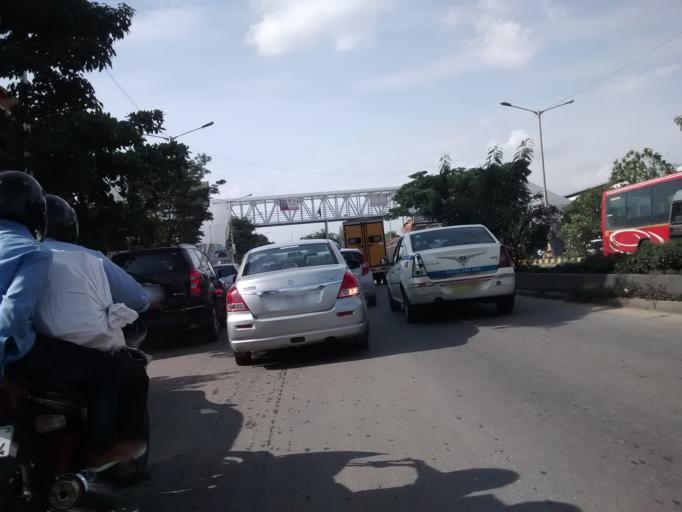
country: IN
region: Karnataka
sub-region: Bangalore Urban
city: Bangalore
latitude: 13.0033
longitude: 77.6632
